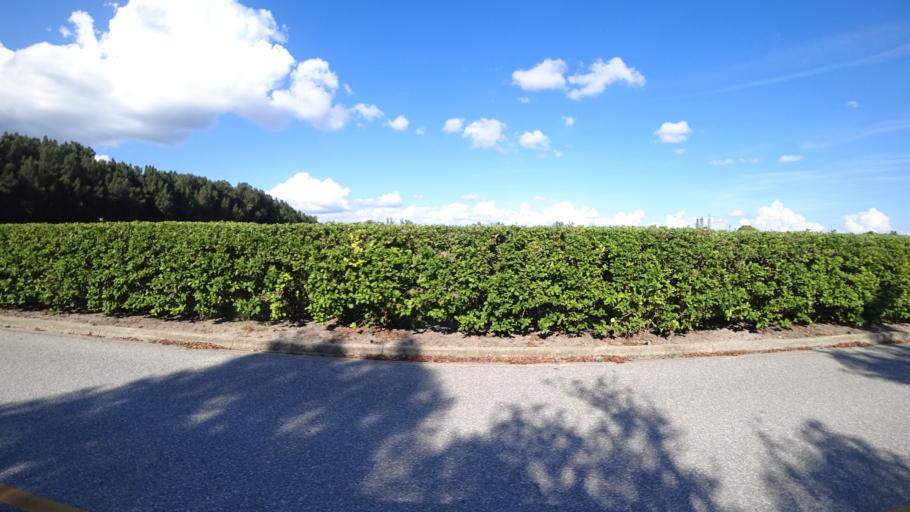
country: US
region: Florida
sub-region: Manatee County
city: Cortez
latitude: 27.4714
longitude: -82.6832
